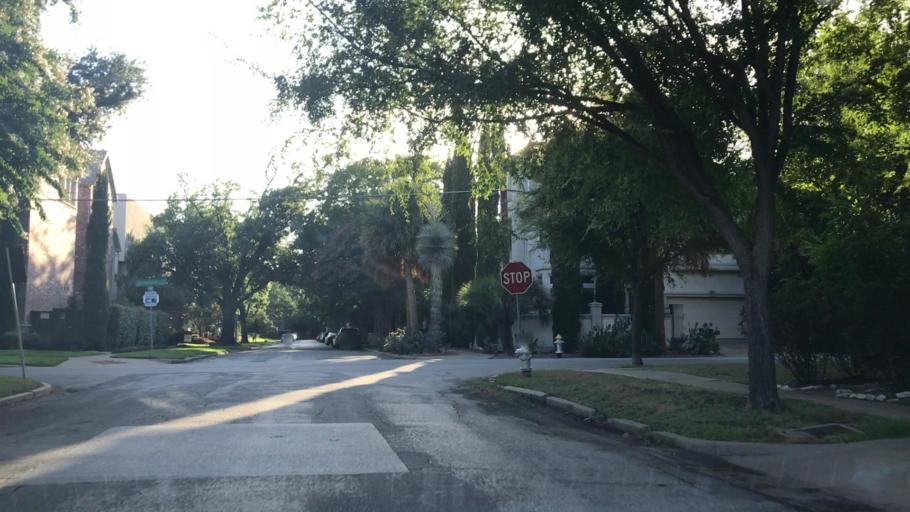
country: US
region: Texas
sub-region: Dallas County
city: Highland Park
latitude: 32.8186
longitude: -96.8042
